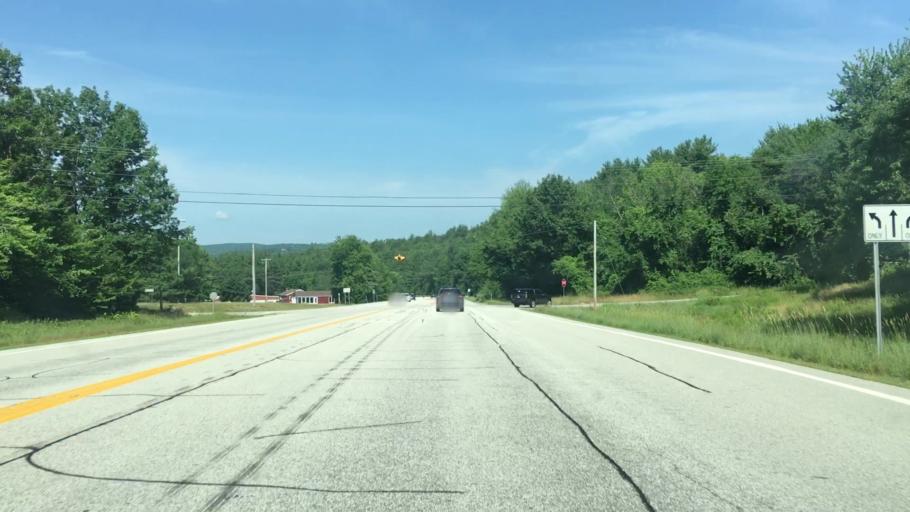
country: US
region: New Hampshire
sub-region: Merrimack County
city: Henniker
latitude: 43.1844
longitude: -71.7872
